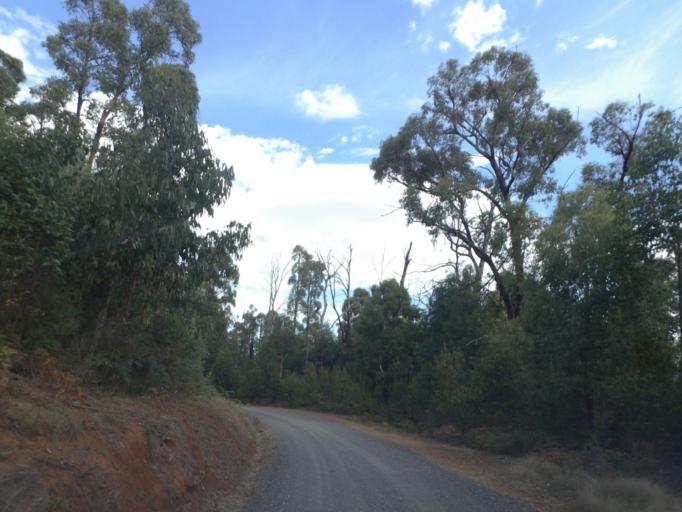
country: AU
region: Victoria
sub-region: Murrindindi
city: Alexandra
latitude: -37.4358
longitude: 145.7587
